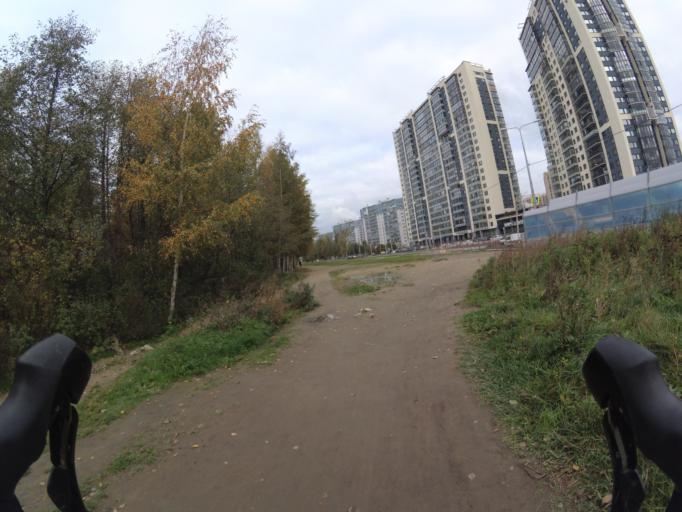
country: RU
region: Leningrad
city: Untolovo
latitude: 59.9935
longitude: 30.1914
